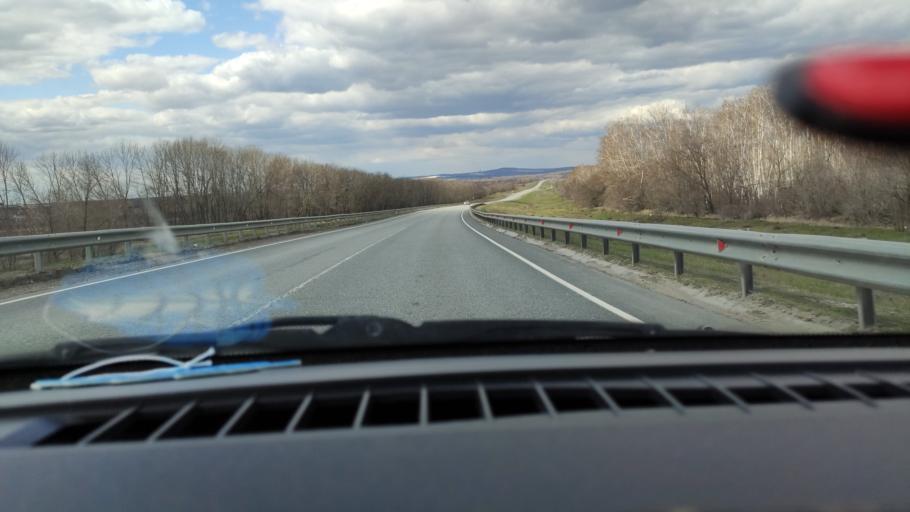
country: RU
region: Saratov
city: Tersa
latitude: 52.0834
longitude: 47.6588
